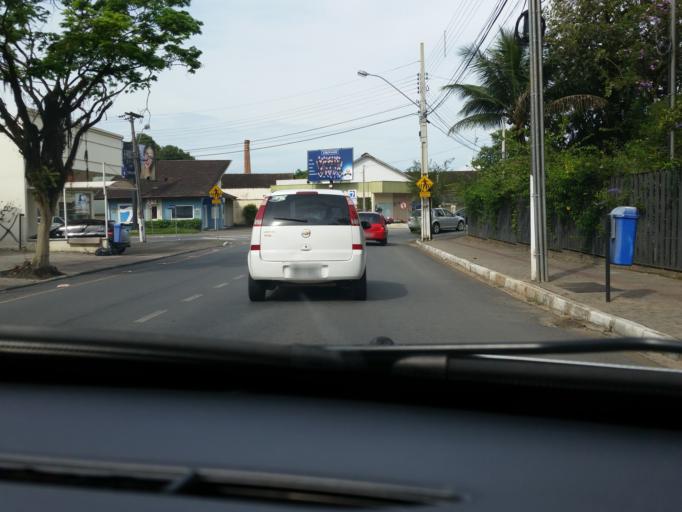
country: BR
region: Santa Catarina
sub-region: Indaial
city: Indaial
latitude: -26.8940
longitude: -49.2404
